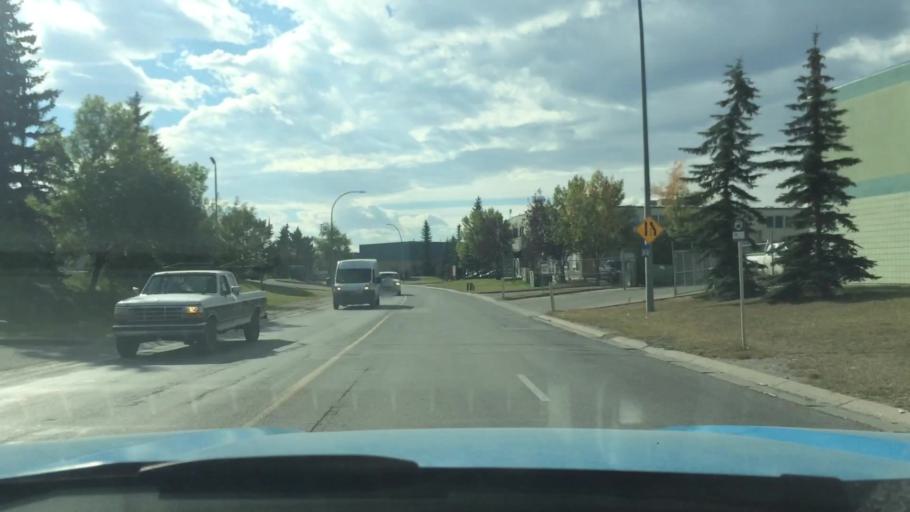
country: CA
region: Alberta
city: Calgary
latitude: 51.0112
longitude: -114.0355
